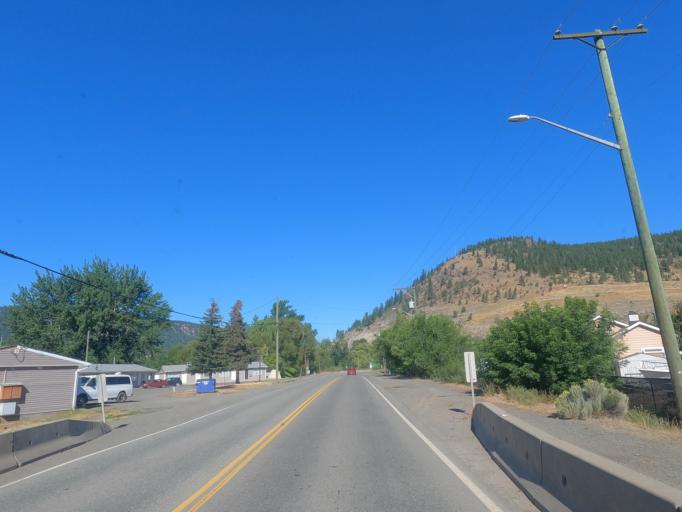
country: CA
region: British Columbia
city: Merritt
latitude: 50.1140
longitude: -120.7967
